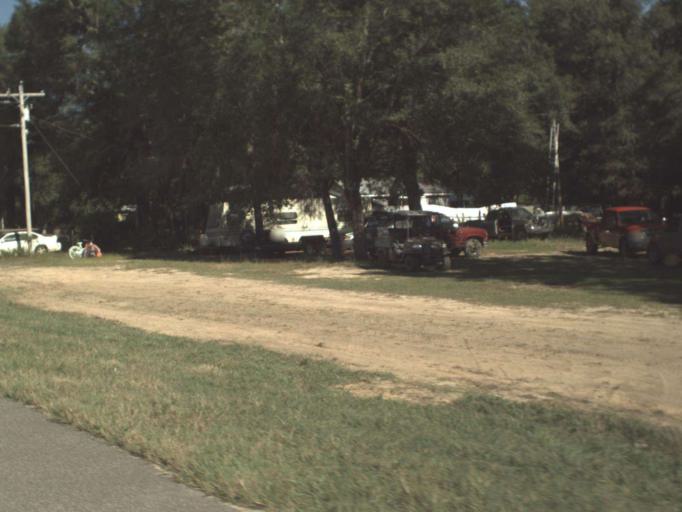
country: US
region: Florida
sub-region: Walton County
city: Freeport
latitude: 30.5823
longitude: -85.9343
